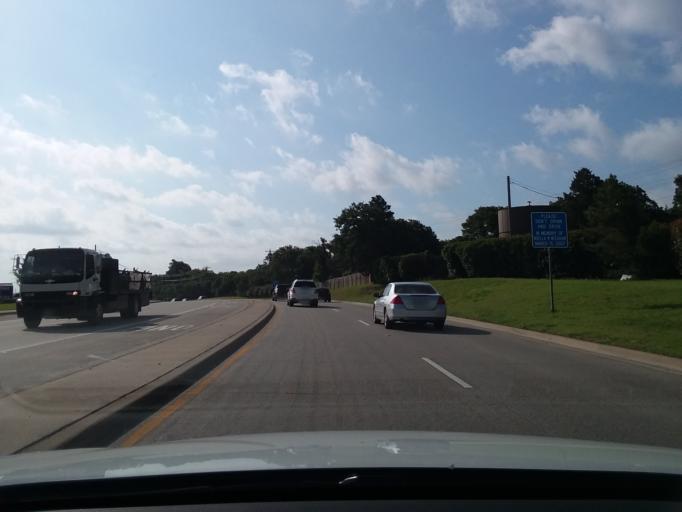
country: US
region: Texas
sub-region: Denton County
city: Double Oak
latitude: 33.0727
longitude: -97.1135
